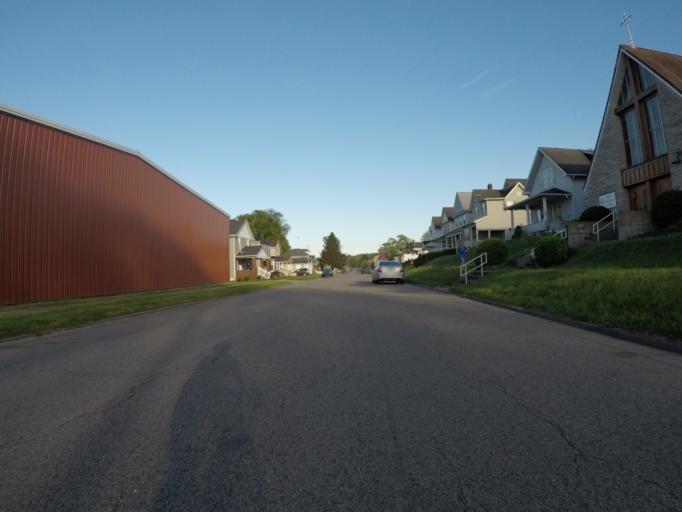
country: US
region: West Virginia
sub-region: Wayne County
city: Kenova
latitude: 38.3982
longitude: -82.5745
